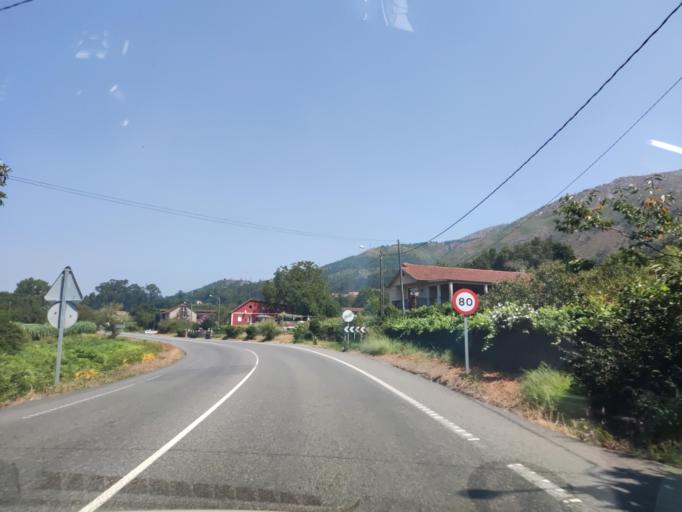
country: ES
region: Galicia
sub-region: Provincia de Pontevedra
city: Redondela
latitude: 42.2250
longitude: -8.5964
